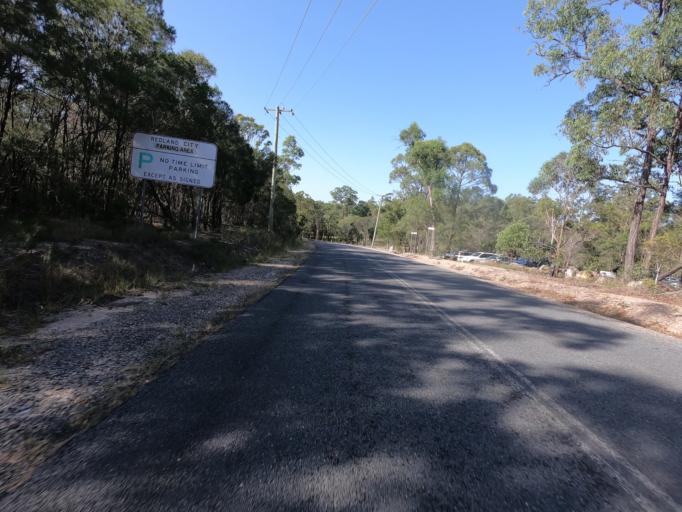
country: AU
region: Queensland
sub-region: Logan
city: Slacks Creek
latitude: -27.6089
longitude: 153.1836
